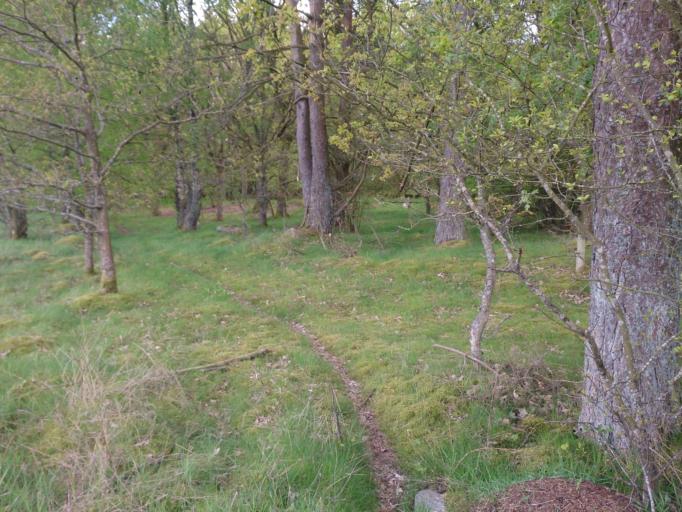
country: SE
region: Skane
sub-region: Sjobo Kommun
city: Sjoebo
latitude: 55.5614
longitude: 13.6961
